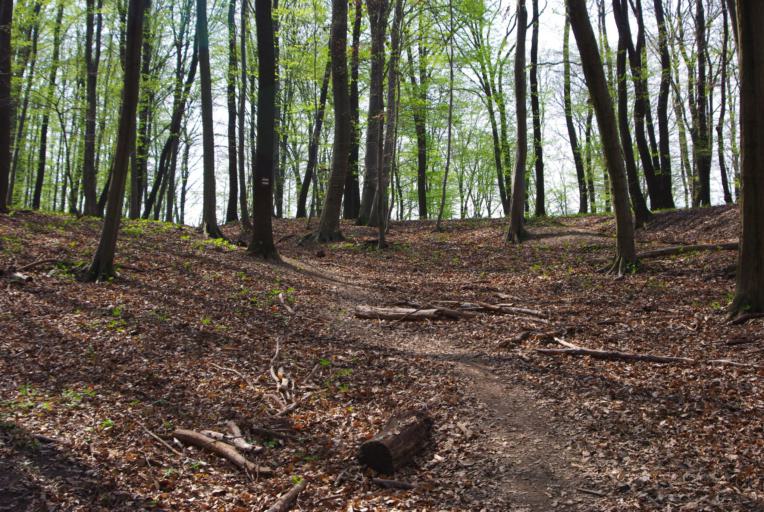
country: HU
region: Fejer
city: Csakvar
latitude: 47.4487
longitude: 18.4383
